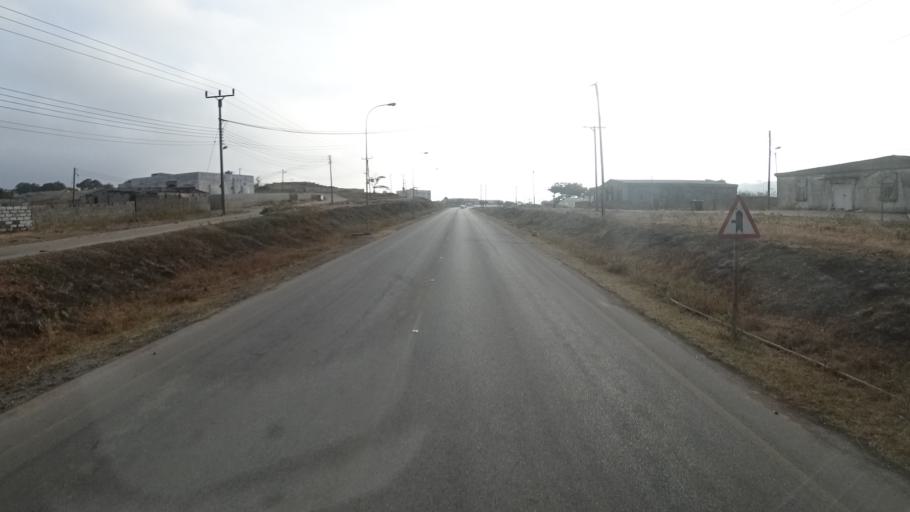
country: OM
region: Zufar
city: Salalah
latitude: 17.1202
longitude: 53.9902
